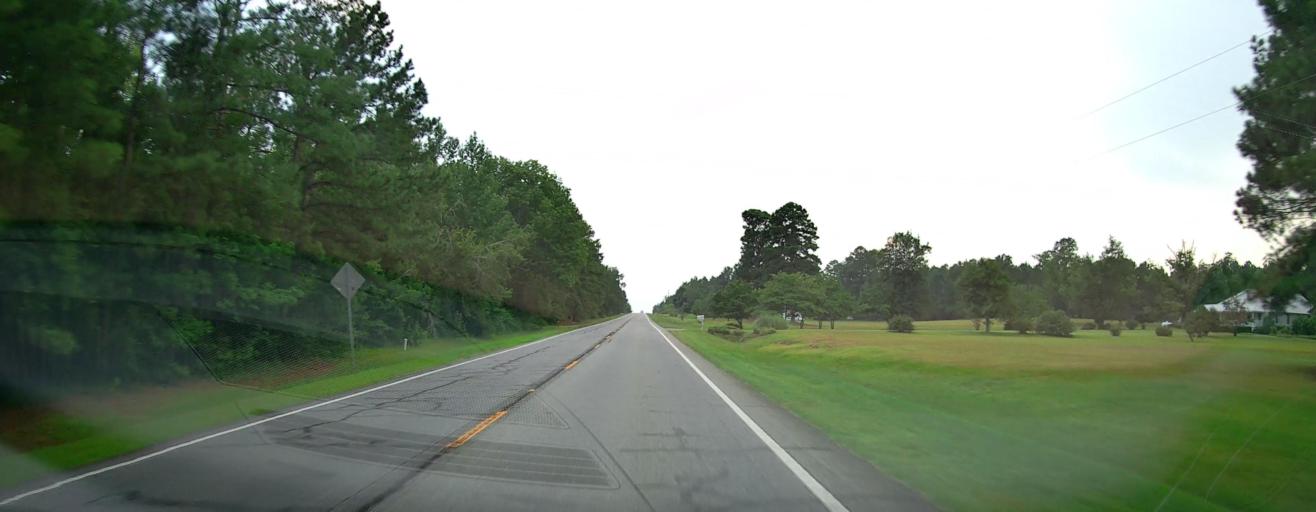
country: US
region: Georgia
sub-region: Laurens County
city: East Dublin
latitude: 32.6288
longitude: -82.8091
